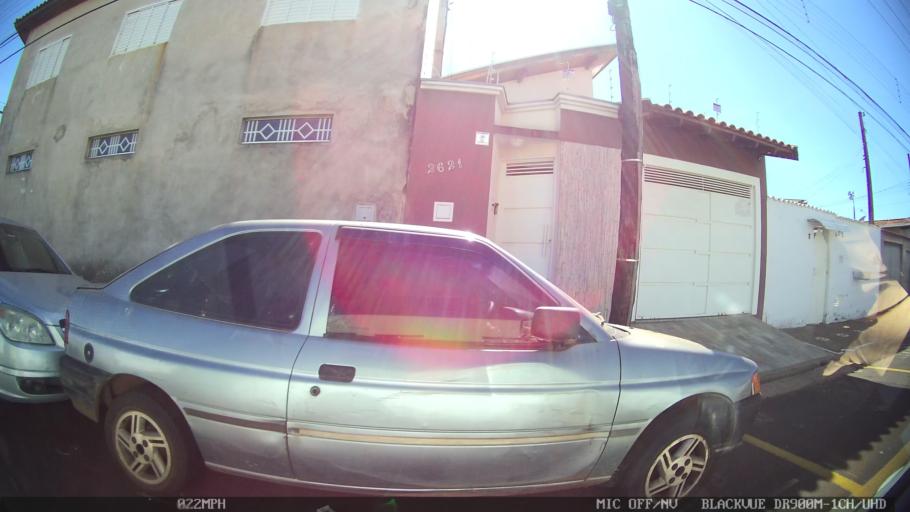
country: BR
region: Sao Paulo
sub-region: Franca
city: Franca
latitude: -20.5470
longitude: -47.3835
